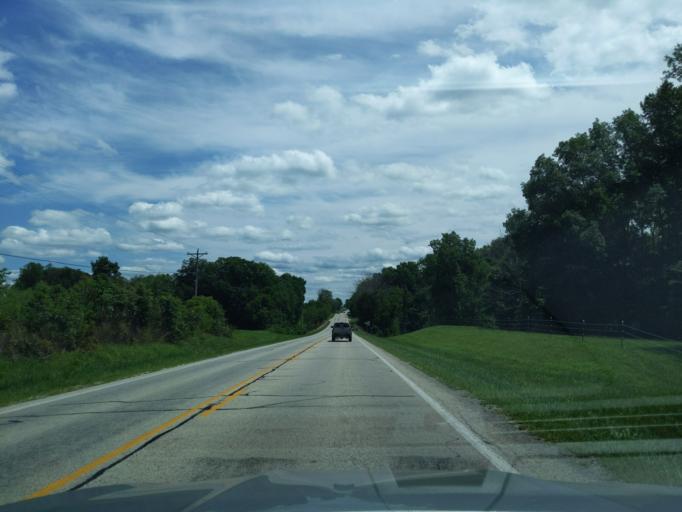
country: US
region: Indiana
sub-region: Ripley County
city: Batesville
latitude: 39.3090
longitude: -85.3051
